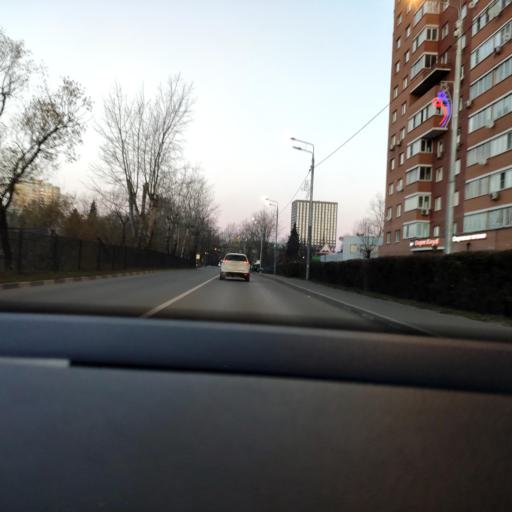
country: RU
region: Moskovskaya
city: Kotel'niki
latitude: 55.6594
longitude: 37.8545
